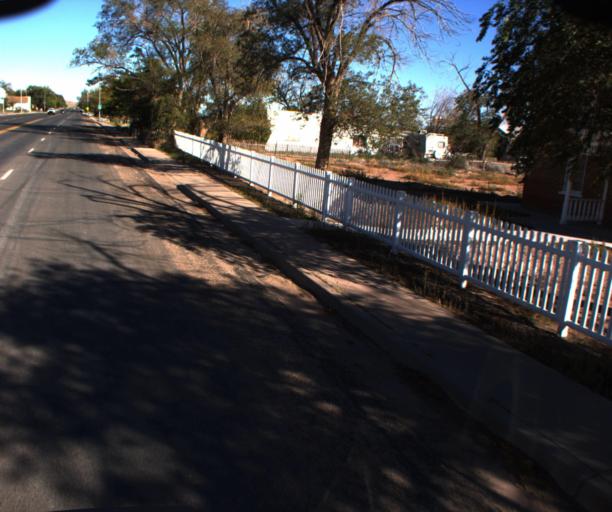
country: US
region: Arizona
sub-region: Navajo County
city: Joseph City
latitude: 34.9560
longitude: -110.3376
